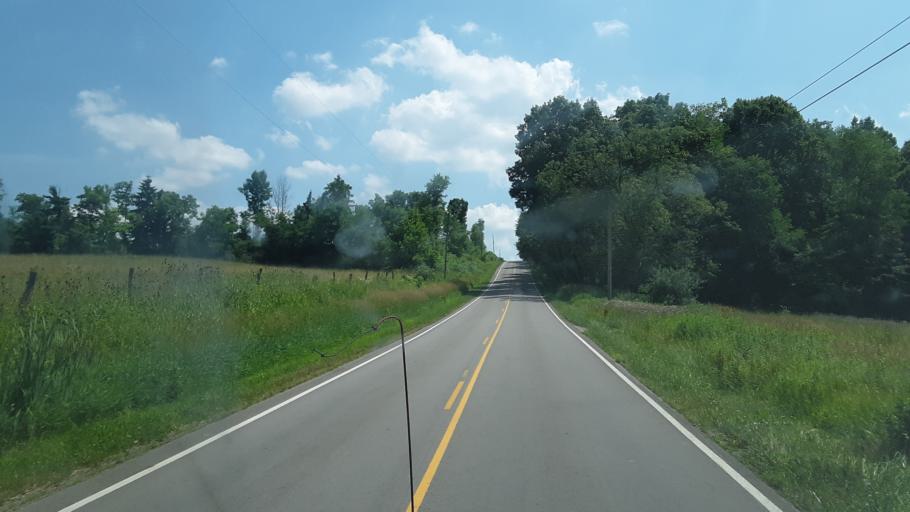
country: US
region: Ohio
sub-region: Stark County
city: Navarre
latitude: 40.6789
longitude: -81.4722
